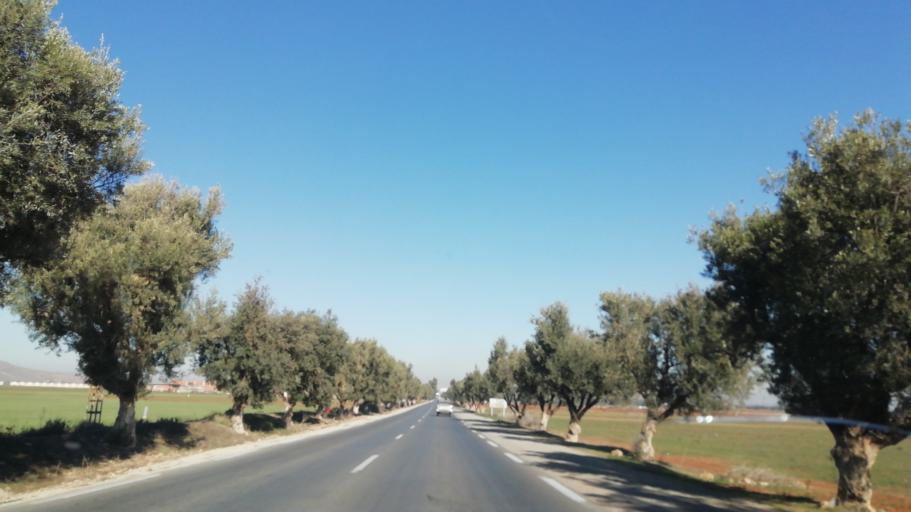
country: DZ
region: Mascara
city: Mascara
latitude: 35.2695
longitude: 0.1287
